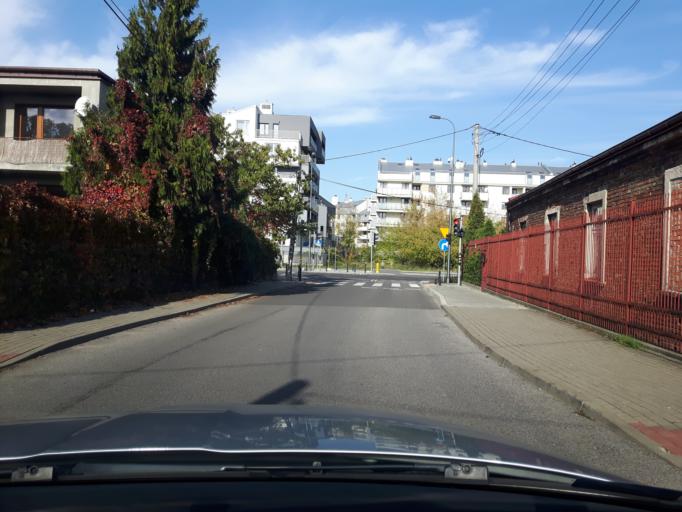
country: PL
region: Masovian Voivodeship
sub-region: Powiat wolominski
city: Zabki
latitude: 52.2863
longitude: 21.0795
